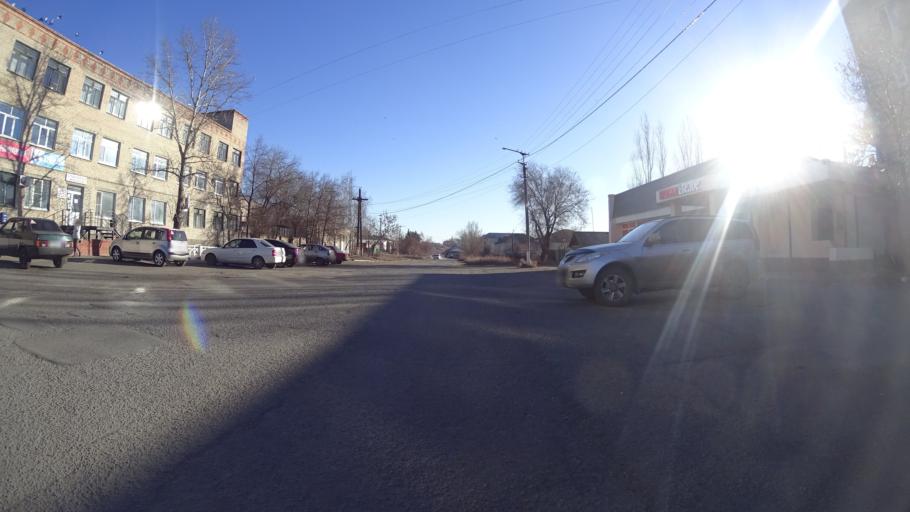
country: RU
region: Chelyabinsk
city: Troitsk
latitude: 54.0871
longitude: 61.5759
